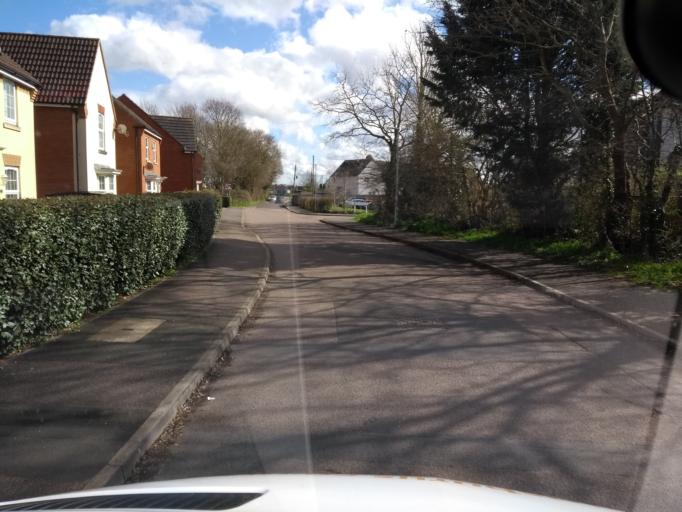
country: GB
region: England
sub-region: Somerset
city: Creech Saint Michael
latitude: 51.0282
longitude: -3.0451
